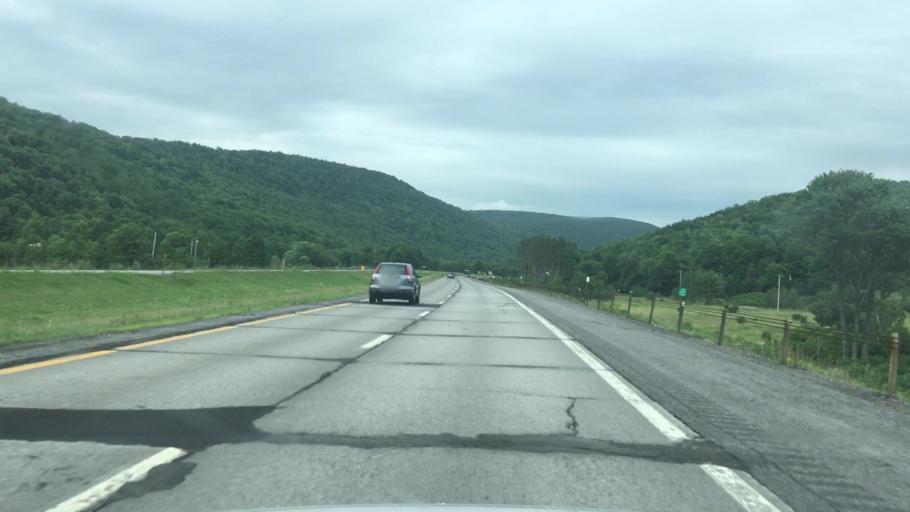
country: US
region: New York
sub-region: Otsego County
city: Worcester
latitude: 42.6259
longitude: -74.6615
